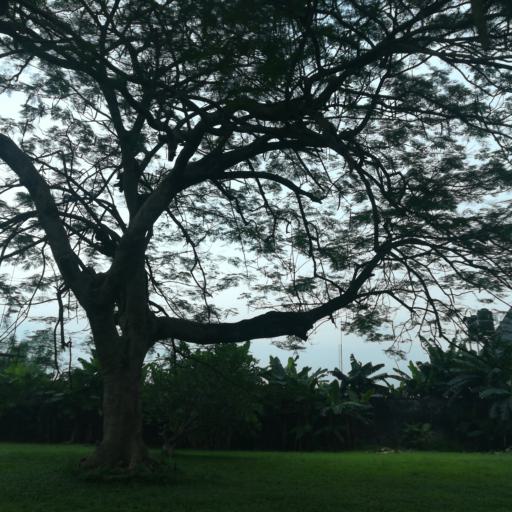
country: NG
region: Rivers
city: Port Harcourt
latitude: 4.7606
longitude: 7.0128
